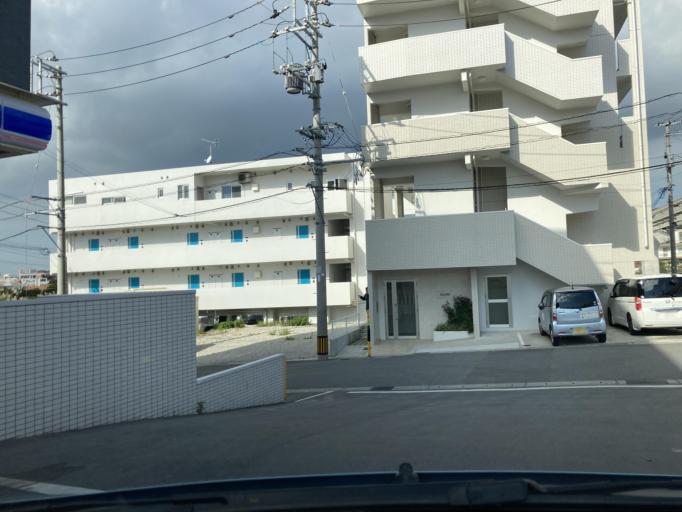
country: JP
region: Okinawa
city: Ginowan
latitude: 26.2414
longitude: 127.7306
